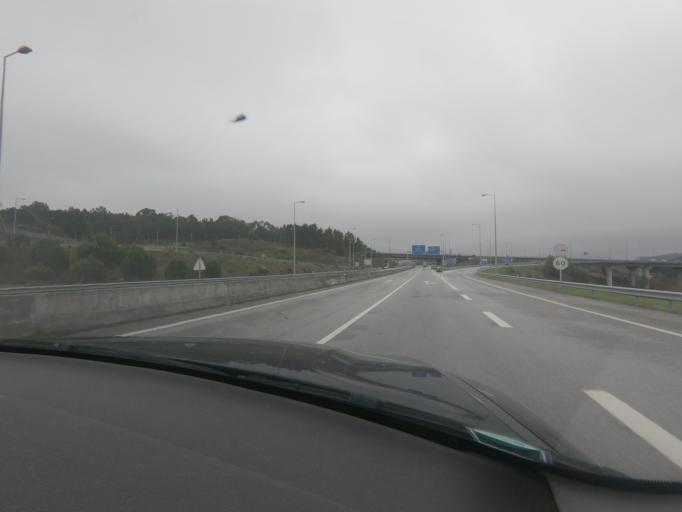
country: PT
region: Viseu
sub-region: Viseu
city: Viseu
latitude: 40.6277
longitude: -7.9610
